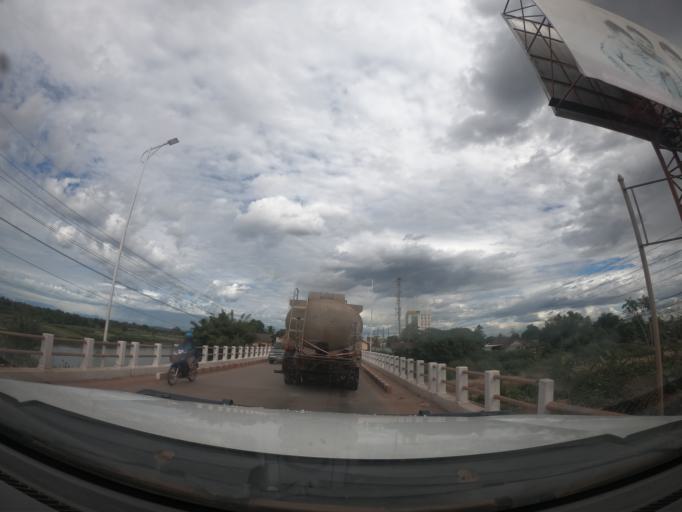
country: LA
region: Bolikhamxai
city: Muang Pakxan
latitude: 18.3947
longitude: 103.6533
